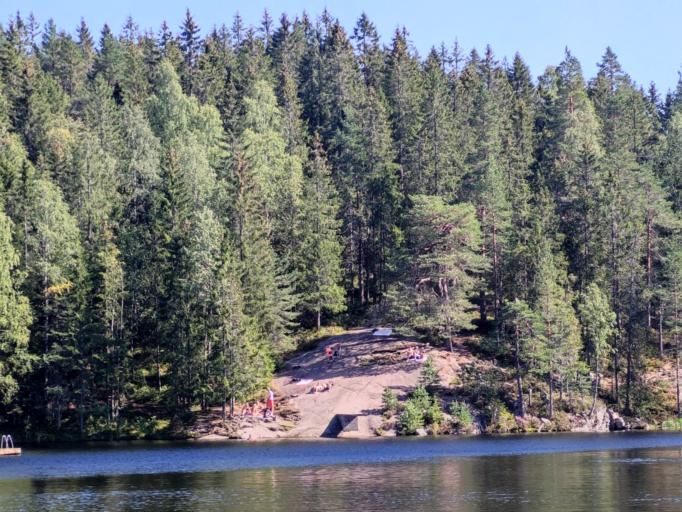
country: NO
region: Akershus
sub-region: Nittedal
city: Rotnes
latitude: 60.0708
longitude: 10.8509
